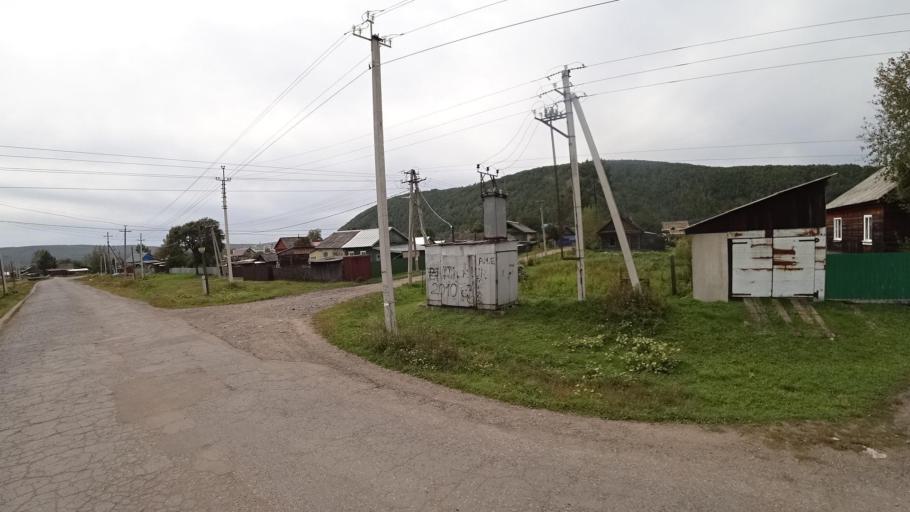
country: RU
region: Jewish Autonomous Oblast
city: Khingansk
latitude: 49.0014
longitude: 131.0542
